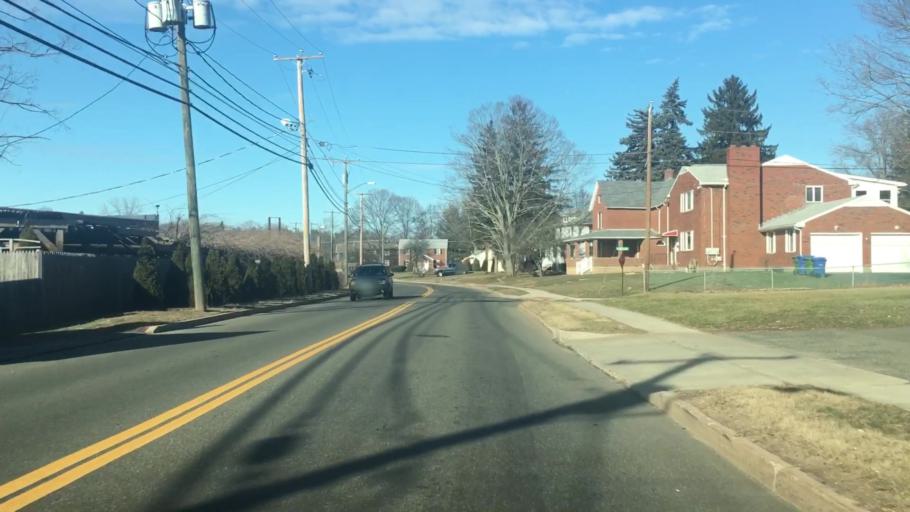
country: US
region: Connecticut
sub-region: Middlesex County
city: Middletown
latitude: 41.5423
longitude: -72.6503
